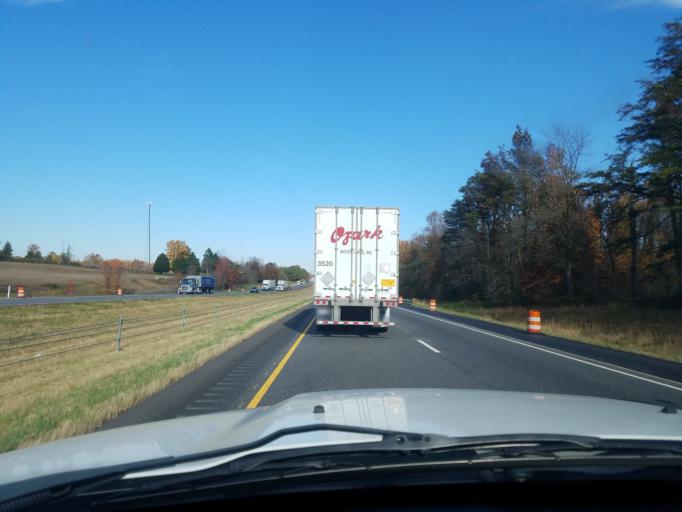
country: US
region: Indiana
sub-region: Scott County
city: Scottsburg
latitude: 38.6317
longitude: -85.7838
